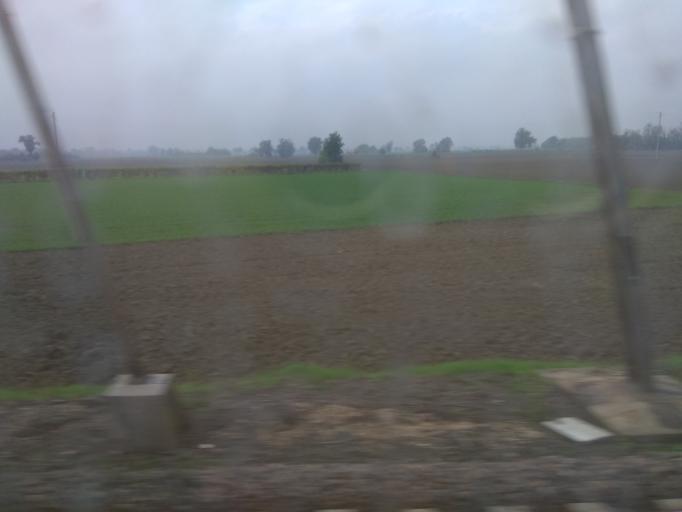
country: IT
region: Piedmont
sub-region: Provincia di Alessandria
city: Pontecurone
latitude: 44.9552
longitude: 8.9228
